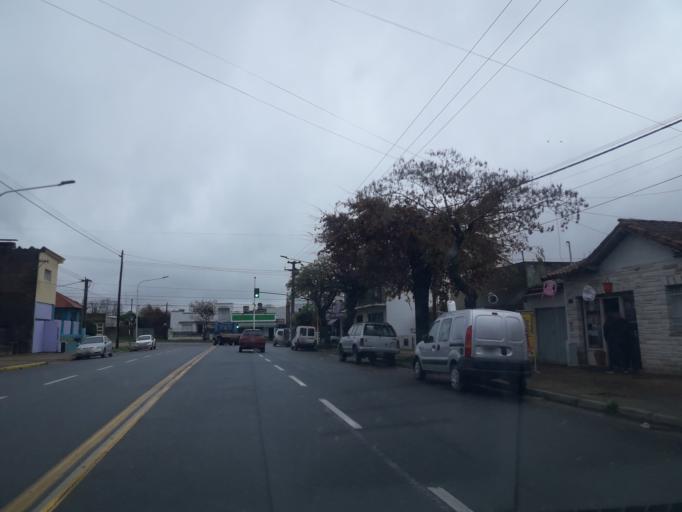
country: AR
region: Buenos Aires
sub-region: Partido de Tandil
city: Tandil
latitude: -37.3171
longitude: -59.1524
